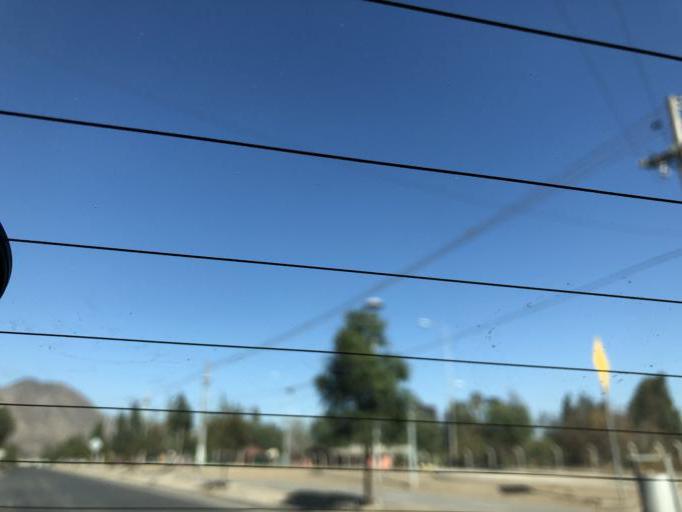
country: CL
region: Santiago Metropolitan
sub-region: Provincia de Santiago
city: La Pintana
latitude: -33.6296
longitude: -70.6289
